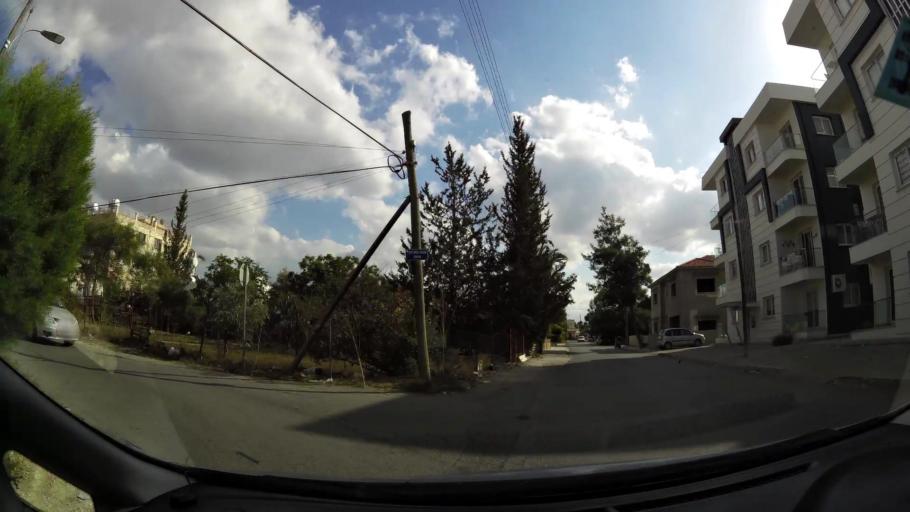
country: CY
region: Lefkosia
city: Nicosia
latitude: 35.1990
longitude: 33.3507
